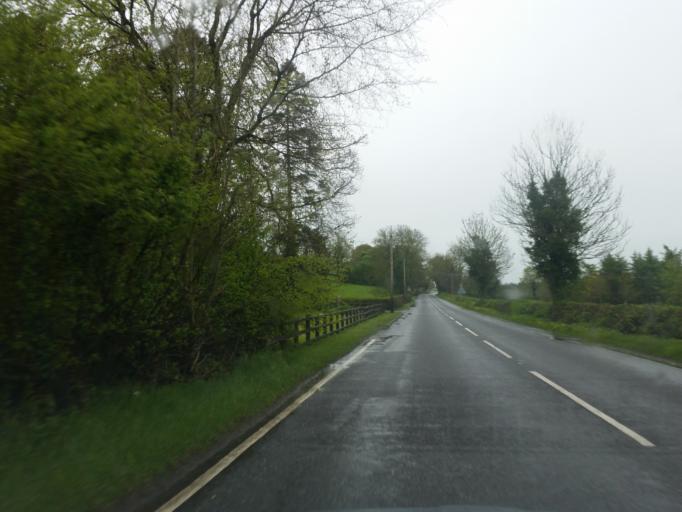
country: GB
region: Northern Ireland
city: Lisnaskea
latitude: 54.2264
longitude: -7.4151
